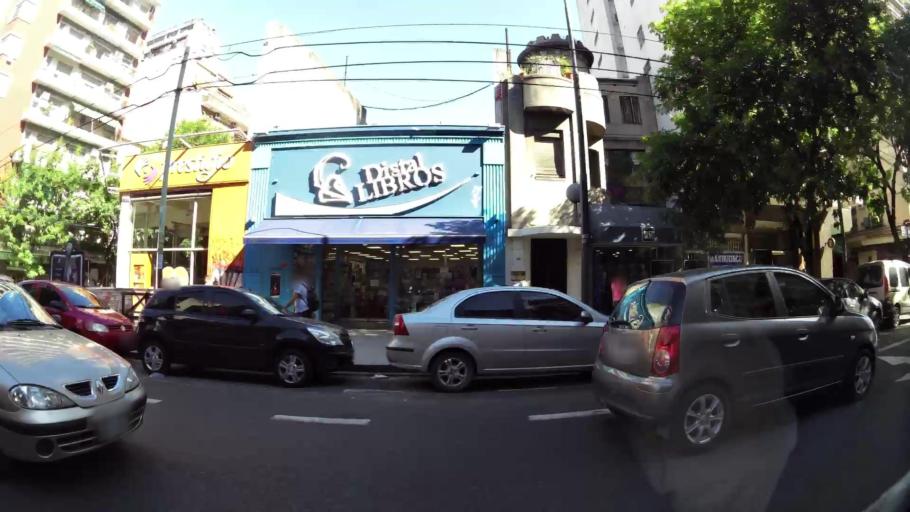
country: AR
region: Buenos Aires F.D.
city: Colegiales
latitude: -34.6160
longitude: -58.4312
